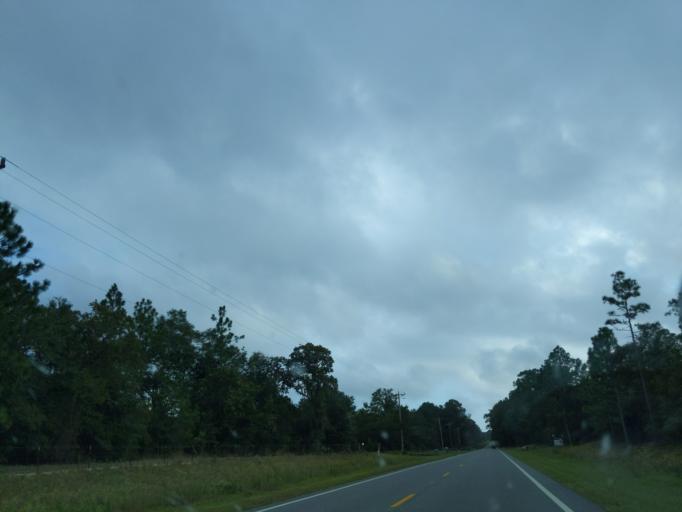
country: US
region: Florida
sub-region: Wakulla County
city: Crawfordville
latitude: 30.1326
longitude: -84.3144
